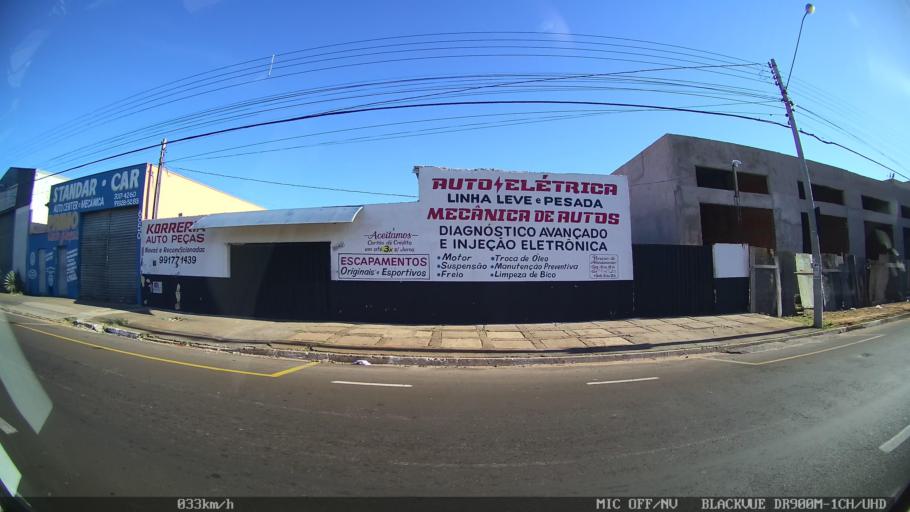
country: BR
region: Sao Paulo
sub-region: Franca
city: Franca
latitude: -20.5716
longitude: -47.3690
